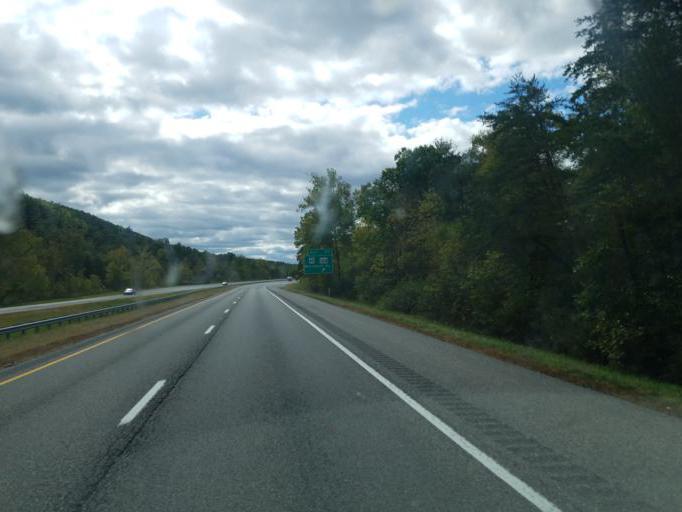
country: US
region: Maryland
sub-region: Washington County
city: Hancock
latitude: 39.7022
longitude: -78.2389
